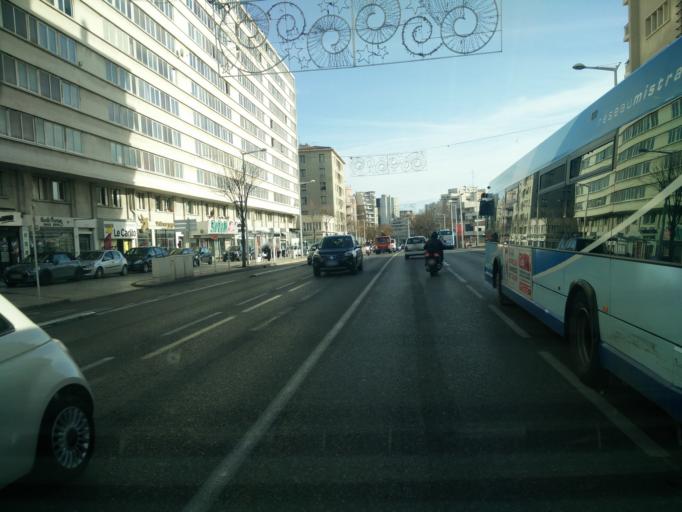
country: FR
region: Provence-Alpes-Cote d'Azur
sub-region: Departement du Var
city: Toulon
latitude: 43.1237
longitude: 5.9371
